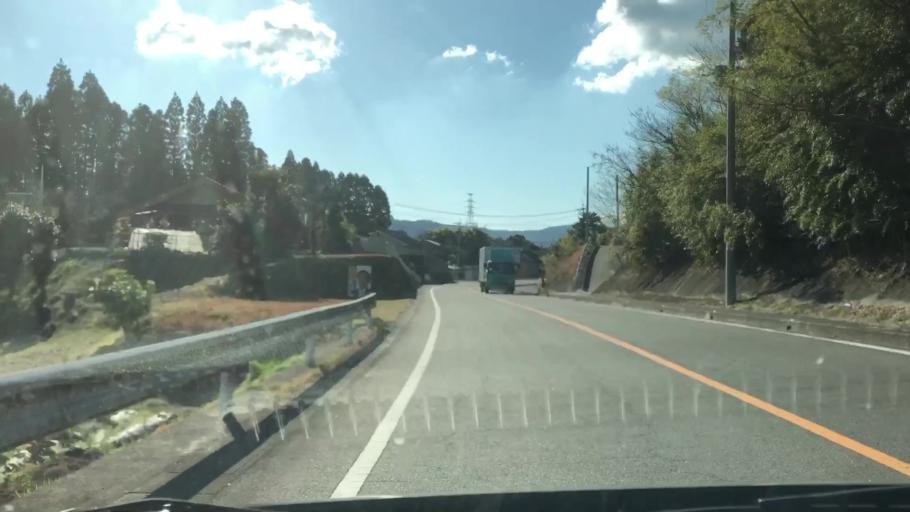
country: JP
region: Kagoshima
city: Satsumasendai
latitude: 31.8578
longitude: 130.3795
